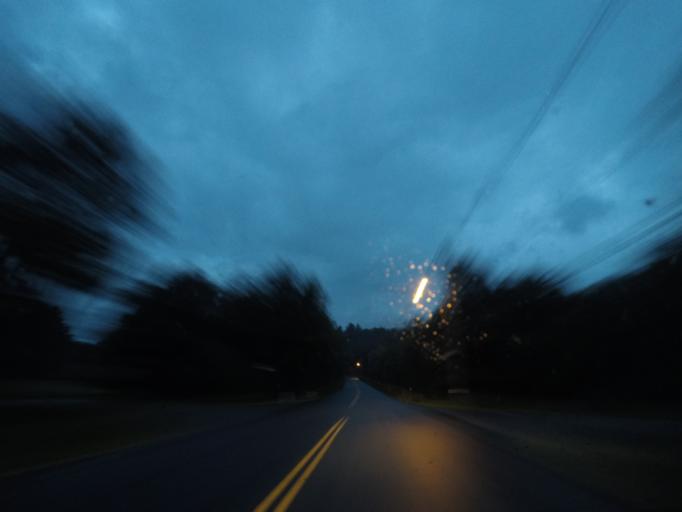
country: US
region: Massachusetts
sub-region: Worcester County
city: Sturbridge
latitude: 42.0750
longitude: -72.0835
